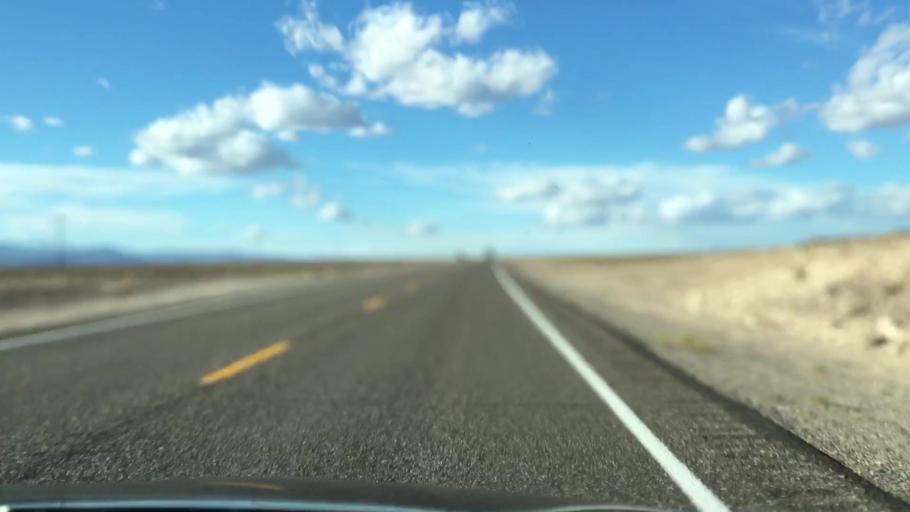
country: US
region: Nevada
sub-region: Nye County
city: Beatty
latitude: 37.1928
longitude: -116.9459
